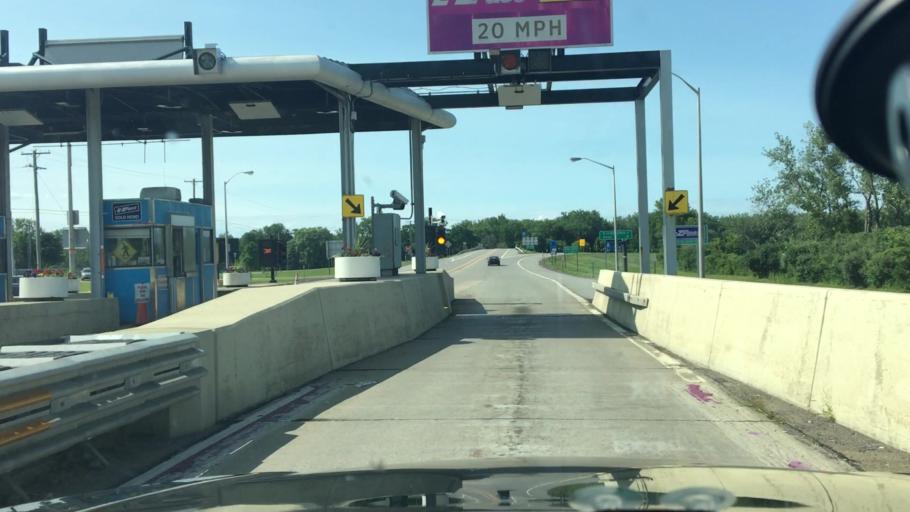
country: US
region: New York
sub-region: Chautauqua County
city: Silver Creek
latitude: 42.5599
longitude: -79.1152
